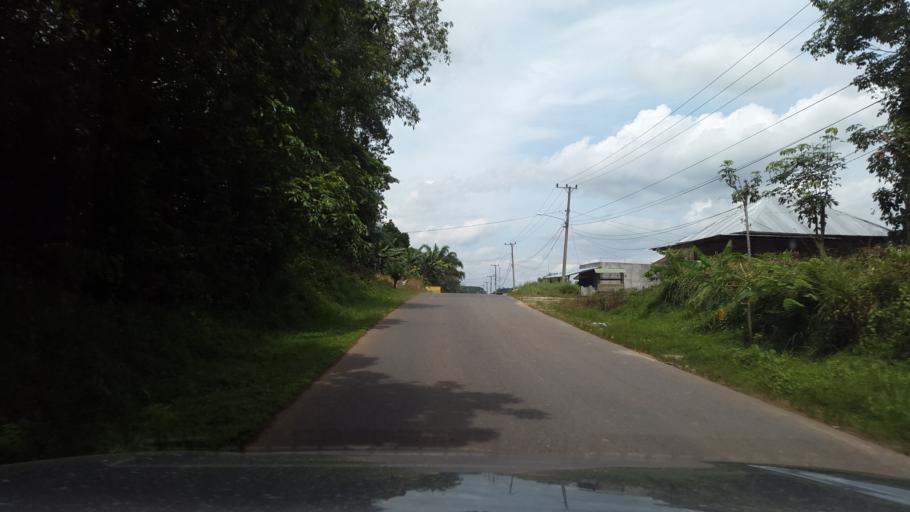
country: ID
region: South Sumatra
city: Gunungmegang Dalam
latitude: -3.3439
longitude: 103.9148
